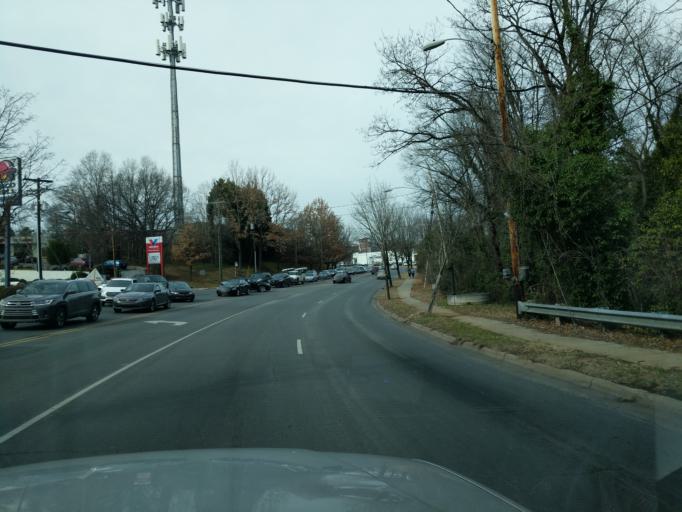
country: US
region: North Carolina
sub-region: Mecklenburg County
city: Charlotte
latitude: 35.1711
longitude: -80.8452
